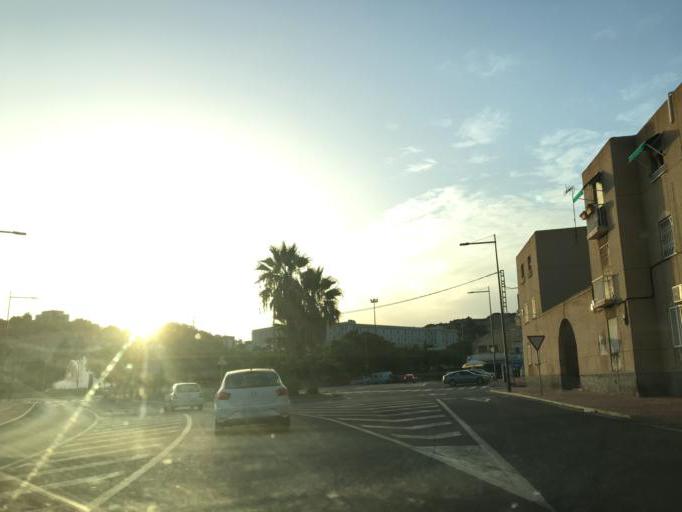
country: ES
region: Murcia
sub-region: Murcia
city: Cartagena
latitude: 37.5994
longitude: -0.9751
